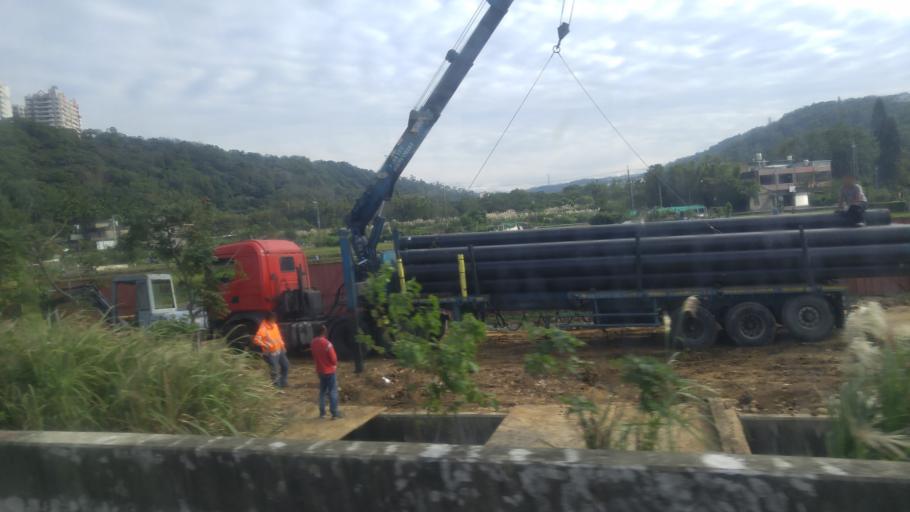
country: TW
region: Taiwan
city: Daxi
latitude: 24.9006
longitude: 121.1525
